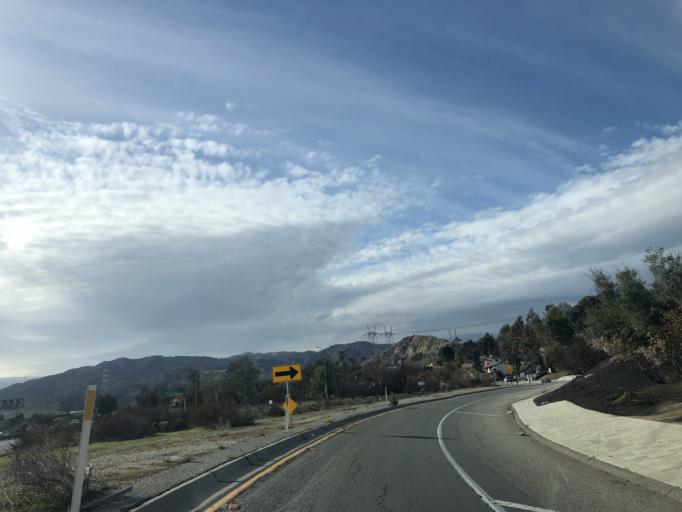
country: US
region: California
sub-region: Los Angeles County
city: San Fernando
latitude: 34.3234
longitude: -118.4770
